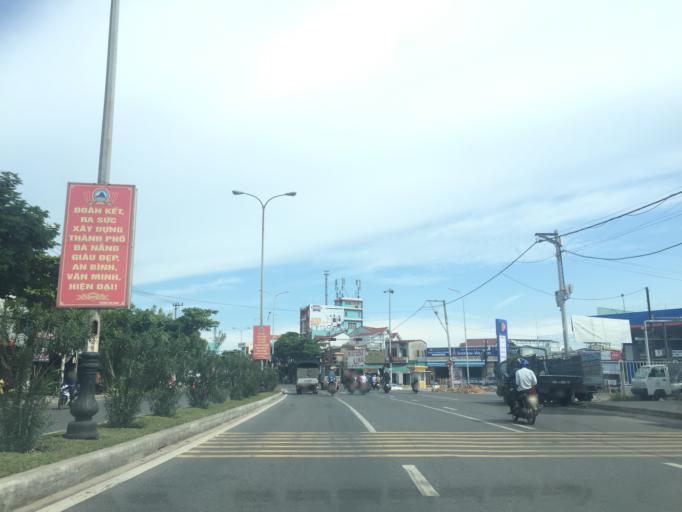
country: VN
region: Da Nang
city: Lien Chieu
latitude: 16.0573
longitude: 108.1666
